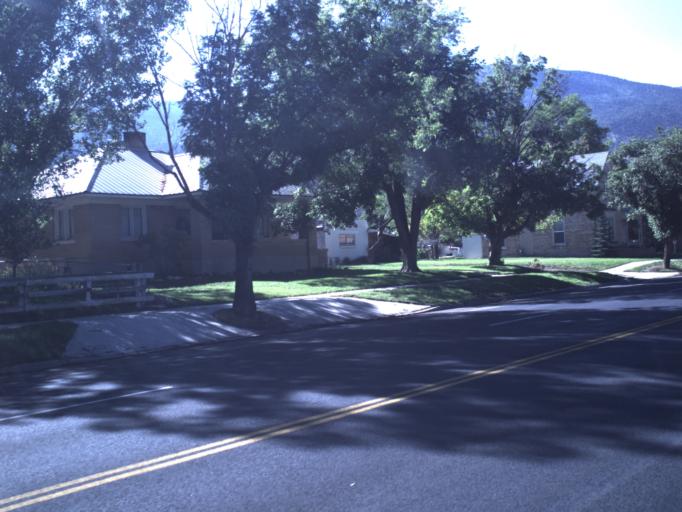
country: US
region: Utah
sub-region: Sanpete County
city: Manti
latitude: 39.2590
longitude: -111.6371
